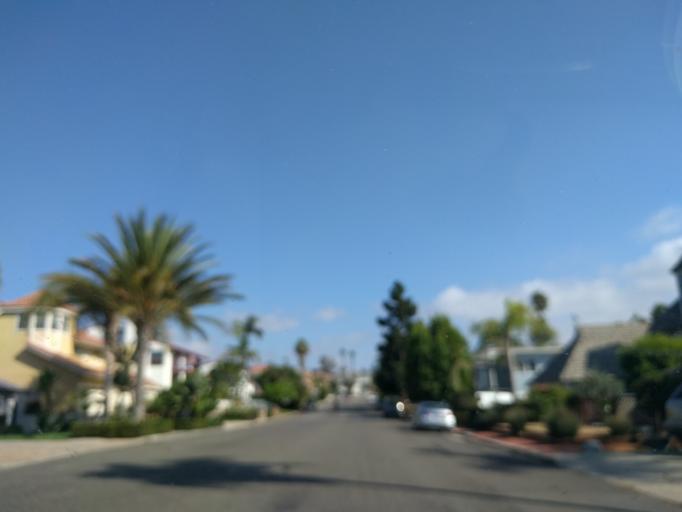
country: US
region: California
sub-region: Orange County
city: Dana Point
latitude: 33.4711
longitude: -117.7053
